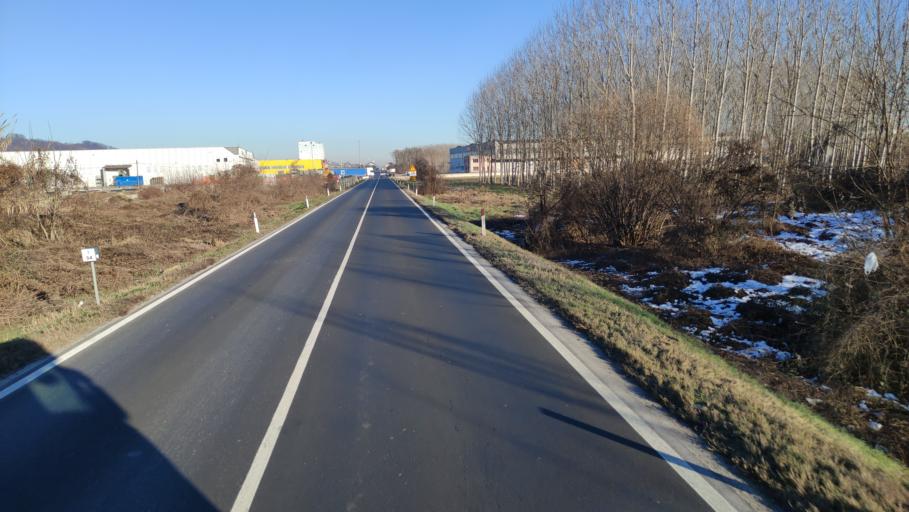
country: IT
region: Piedmont
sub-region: Provincia di Cuneo
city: Borgo
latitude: 44.6969
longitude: 7.9526
